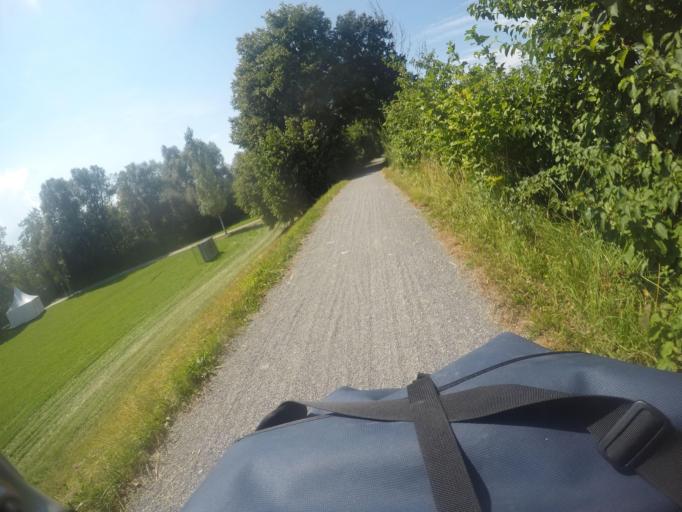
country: CH
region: Saint Gallen
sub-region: Wahlkreis Rheintal
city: Diepoldsau
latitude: 47.3971
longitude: 9.6650
